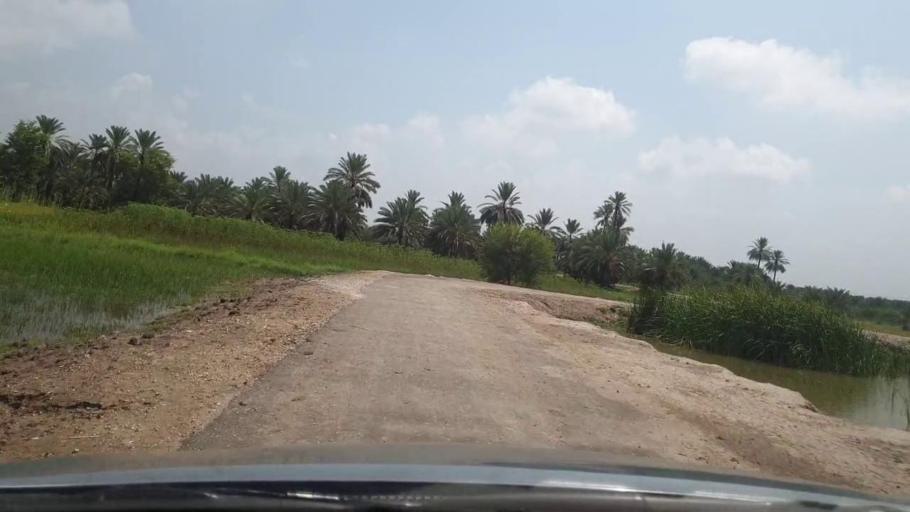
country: PK
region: Sindh
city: Pir jo Goth
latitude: 27.6204
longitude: 68.6644
